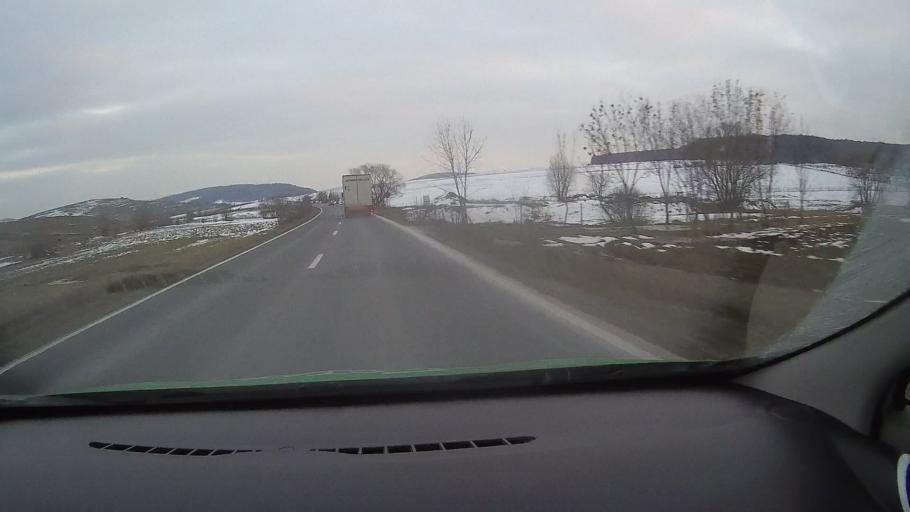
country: RO
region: Harghita
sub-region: Comuna Lupeni
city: Lupeni
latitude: 46.3537
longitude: 25.2542
